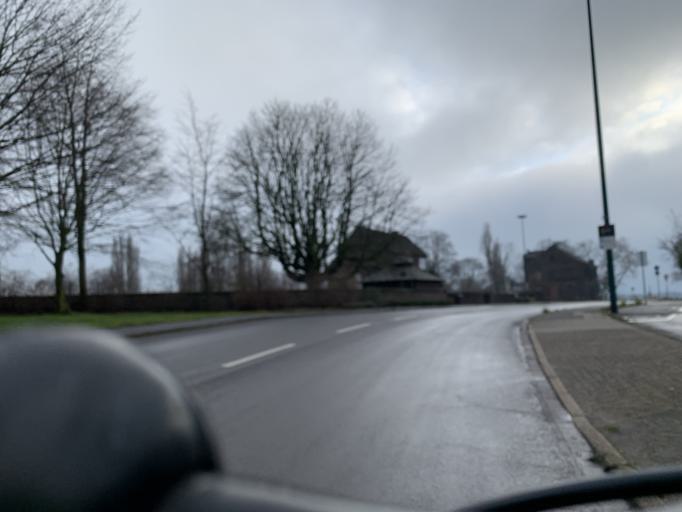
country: DE
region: North Rhine-Westphalia
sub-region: Regierungsbezirk Dusseldorf
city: Krefeld
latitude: 51.3708
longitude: 6.6647
